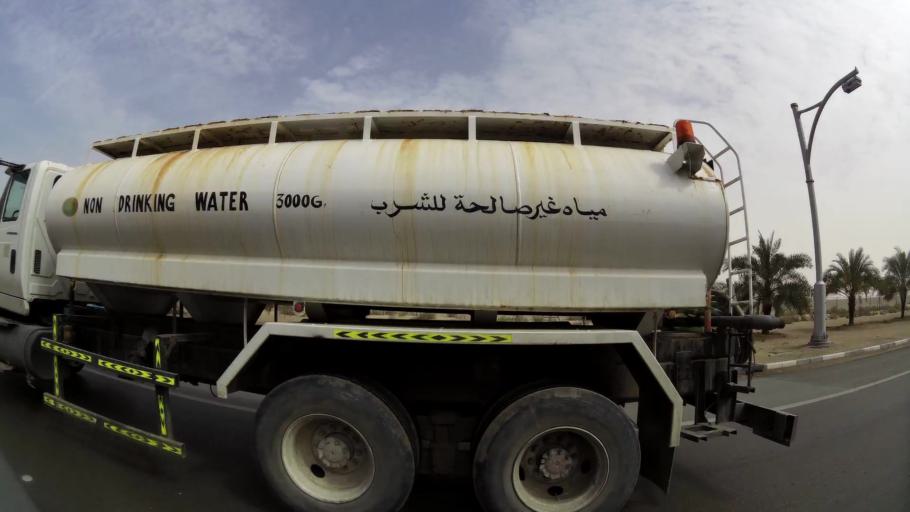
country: AE
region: Abu Dhabi
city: Abu Dhabi
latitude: 24.3661
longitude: 54.5254
